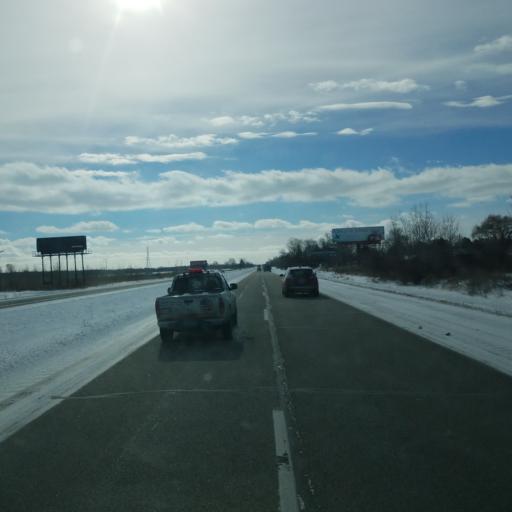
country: US
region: Michigan
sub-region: Gratiot County
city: Ithaca
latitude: 43.2161
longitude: -84.5634
